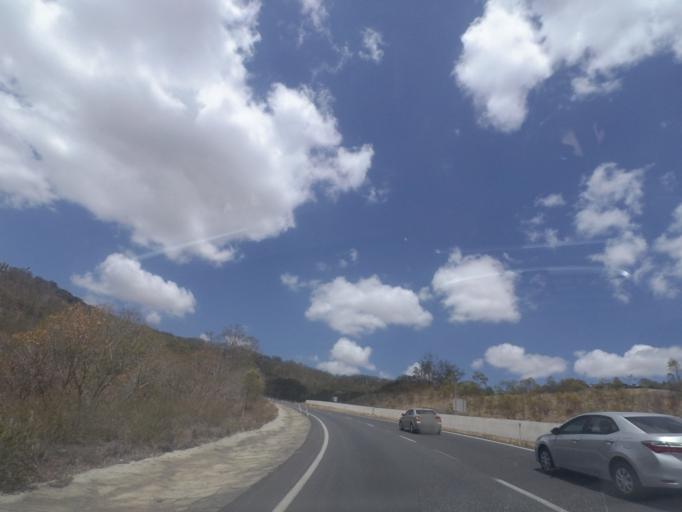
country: AU
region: Queensland
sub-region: Toowoomba
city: East Toowoomba
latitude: -27.5699
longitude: 151.9896
